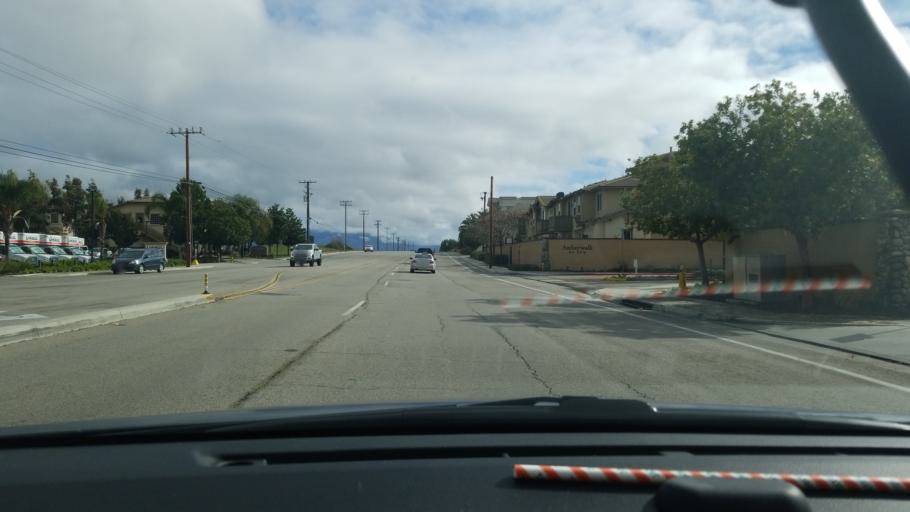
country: US
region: California
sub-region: Riverside County
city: Murrieta
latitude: 33.5554
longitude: -117.2043
